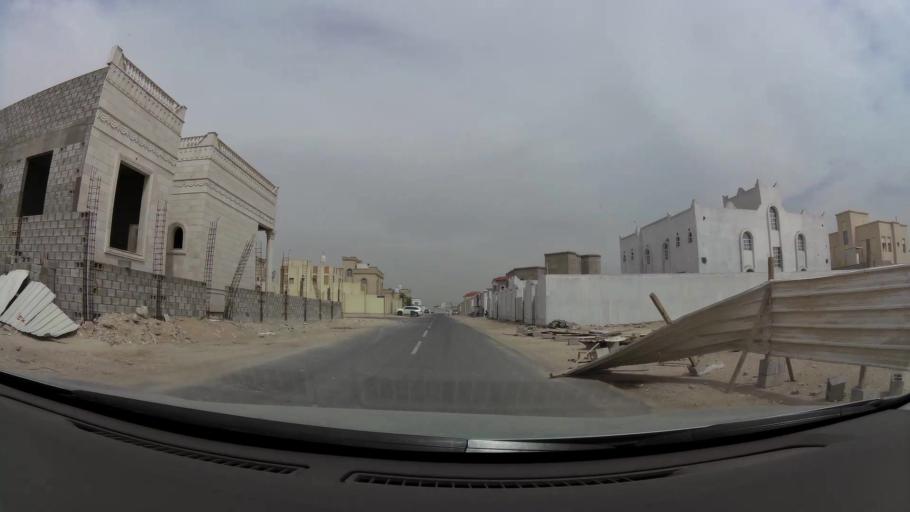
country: QA
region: Baladiyat ar Rayyan
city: Ar Rayyan
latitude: 25.2089
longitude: 51.4513
